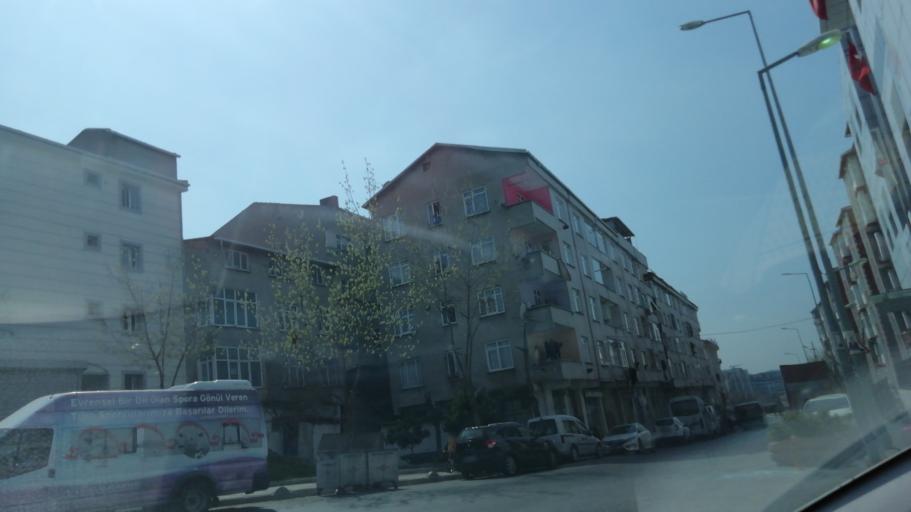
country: TR
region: Istanbul
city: Mahmutbey
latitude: 41.0389
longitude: 28.8222
